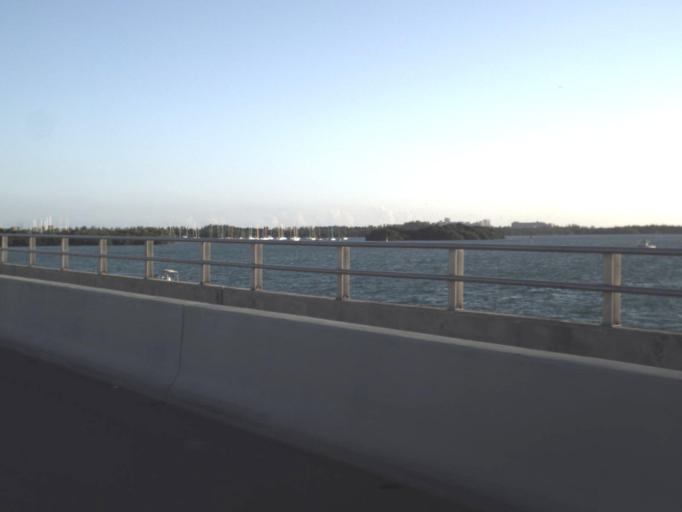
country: US
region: Florida
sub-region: Miami-Dade County
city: Key Biscayne
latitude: 25.7317
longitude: -80.1603
